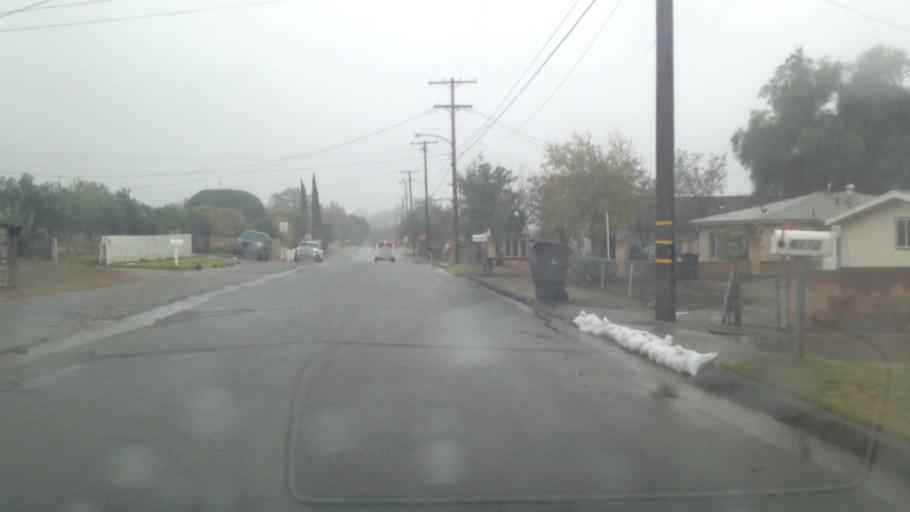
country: US
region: California
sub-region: Riverside County
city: Pedley
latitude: 33.9420
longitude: -117.4868
